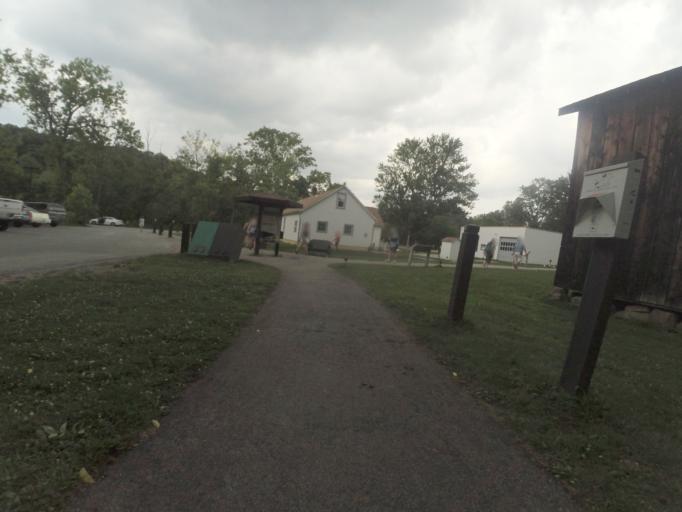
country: US
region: Ohio
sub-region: Summit County
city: Peninsula
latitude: 41.2630
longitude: -81.5585
